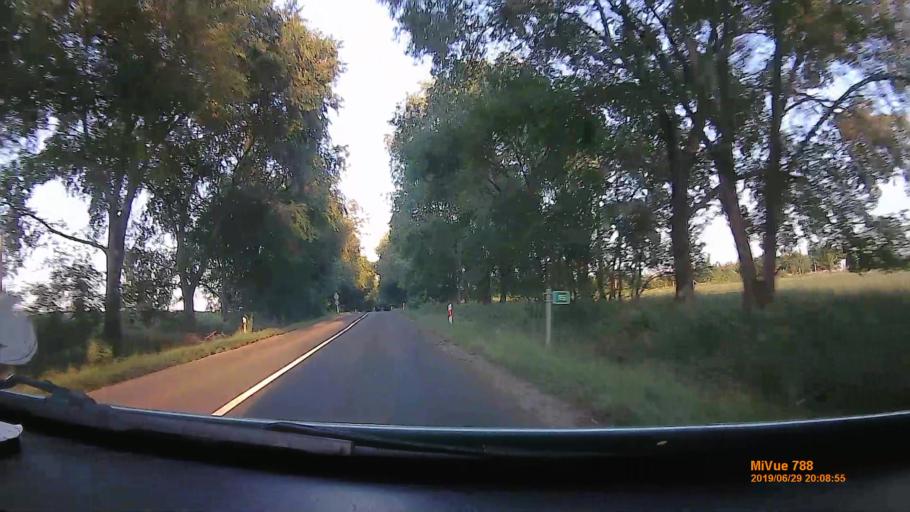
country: HU
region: Pest
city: Zsambek
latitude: 47.5404
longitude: 18.7500
